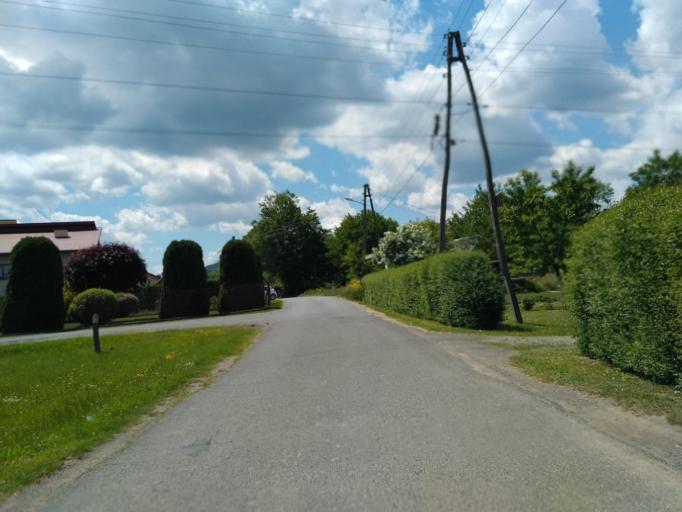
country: PL
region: Subcarpathian Voivodeship
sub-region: Powiat krosnienski
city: Dukla
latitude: 49.5634
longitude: 21.6956
